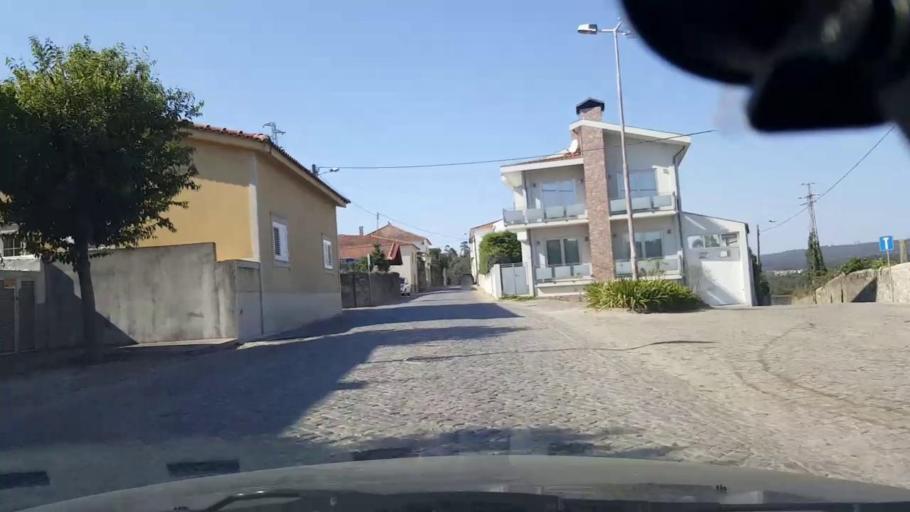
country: PT
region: Porto
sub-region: Vila do Conde
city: Arvore
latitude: 41.3817
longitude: -8.6827
